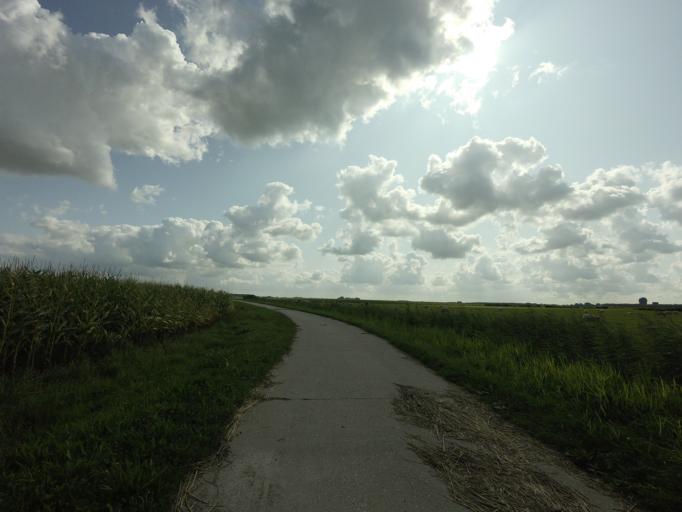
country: NL
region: Friesland
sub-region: Gemeente Het Bildt
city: Sint Jacobiparochie
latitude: 53.2677
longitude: 5.6120
